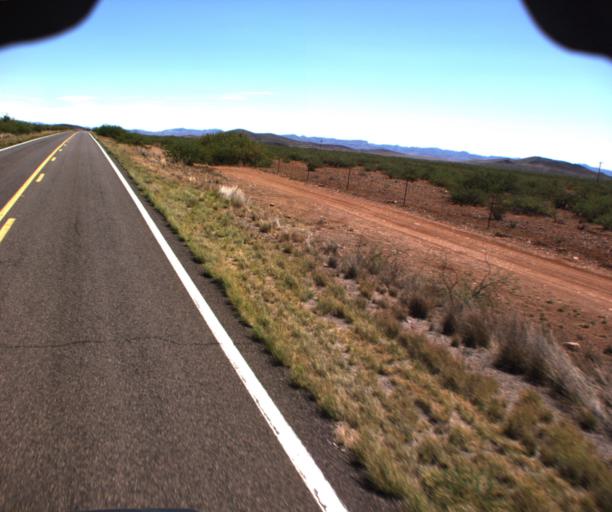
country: US
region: Arizona
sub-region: Cochise County
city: Douglas
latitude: 31.4960
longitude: -109.3330
